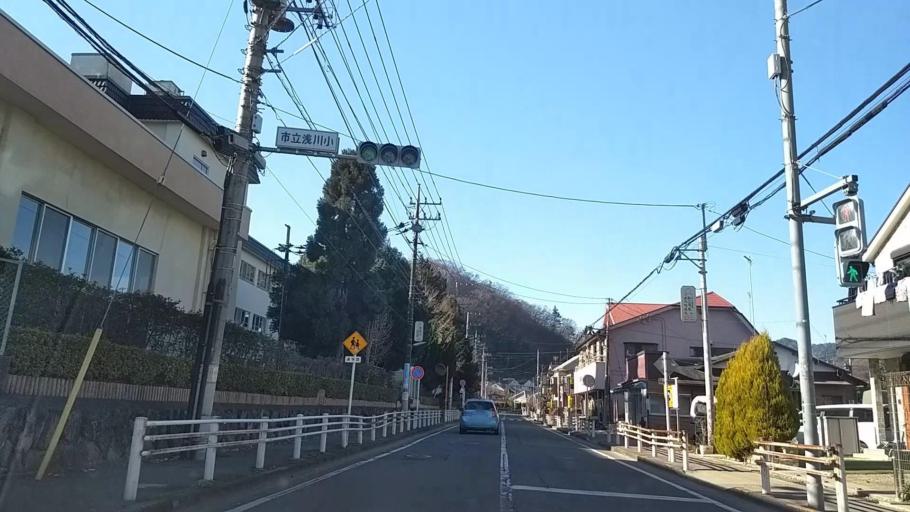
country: JP
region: Tokyo
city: Hachioji
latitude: 35.6408
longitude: 139.2826
